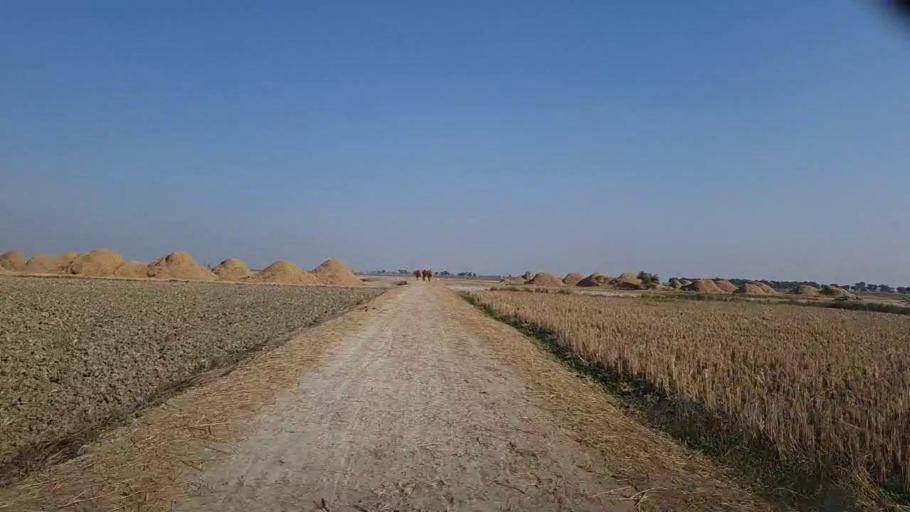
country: PK
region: Sindh
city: Thul
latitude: 28.3590
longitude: 68.7692
